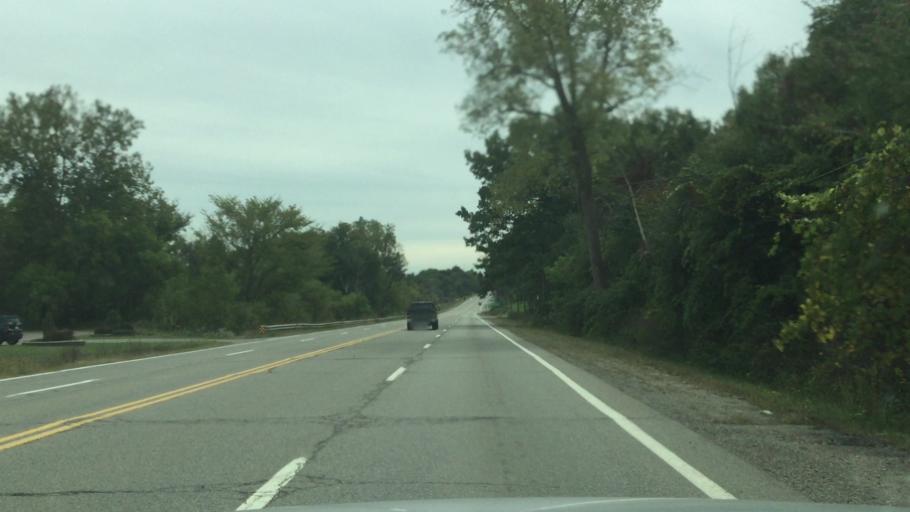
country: US
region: Michigan
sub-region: Oakland County
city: Ortonville
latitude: 42.7835
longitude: -83.5026
